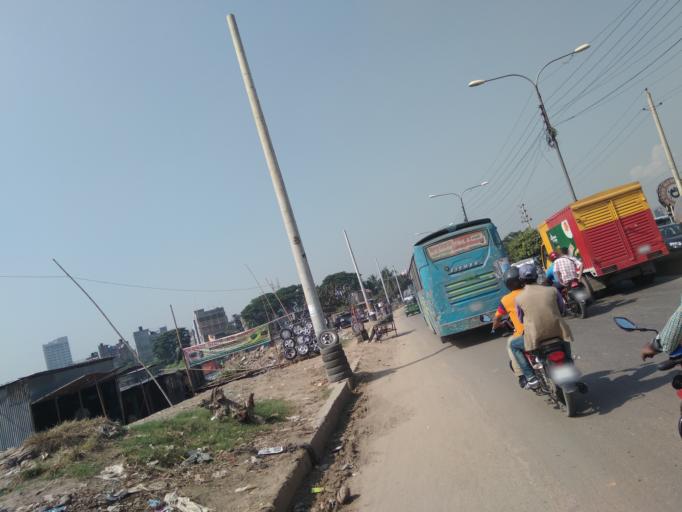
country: BD
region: Dhaka
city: Tungi
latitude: 23.8225
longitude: 90.3818
